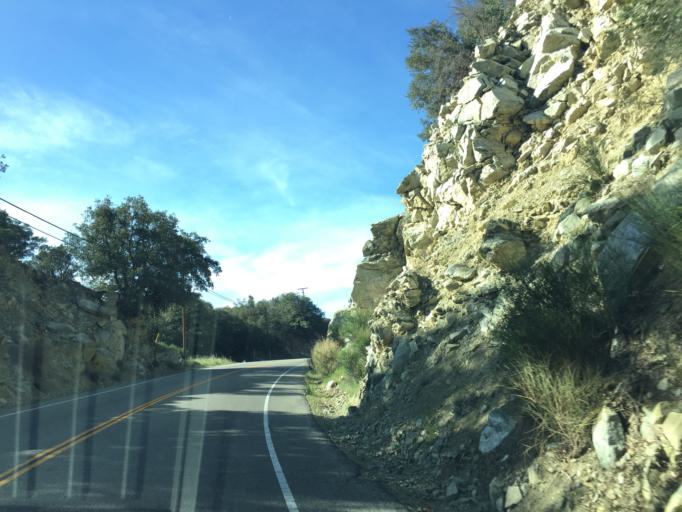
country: US
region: California
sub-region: San Bernardino County
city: San Antonio Heights
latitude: 34.2220
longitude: -117.6679
